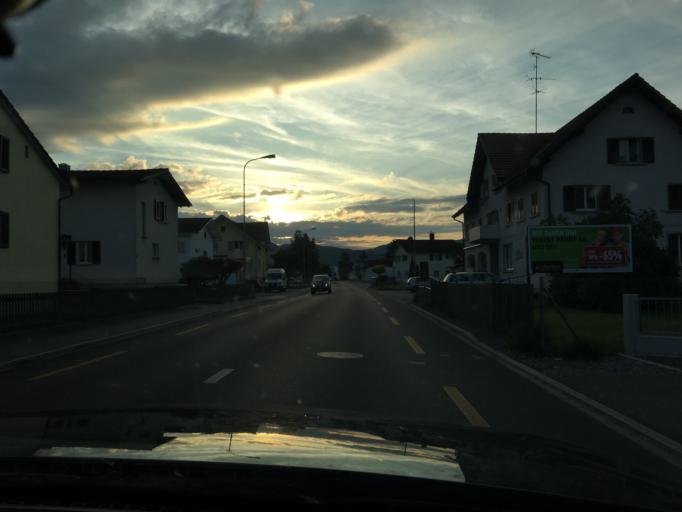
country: CH
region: Saint Gallen
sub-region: Wahlkreis Rheintal
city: Diepoldsau
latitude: 47.3824
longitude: 9.6617
